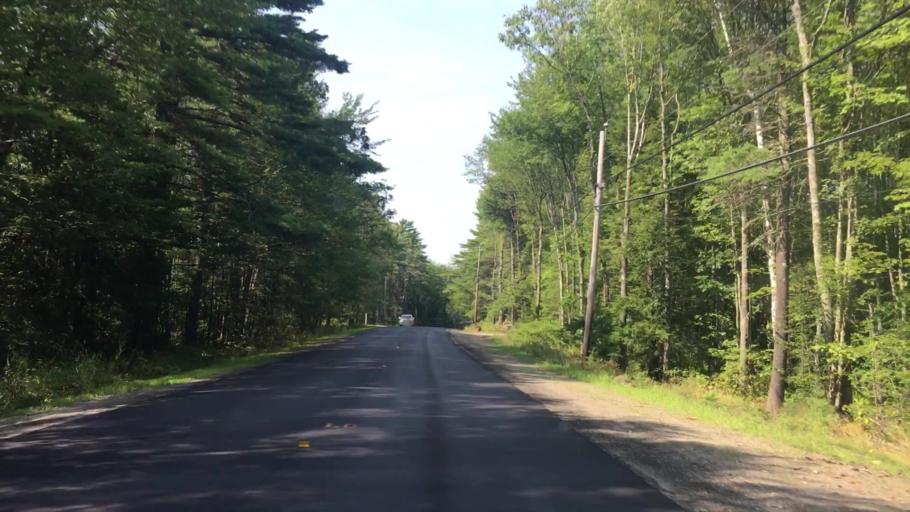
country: US
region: Maine
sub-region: Sagadahoc County
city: North Bath
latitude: 43.9359
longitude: -69.7993
